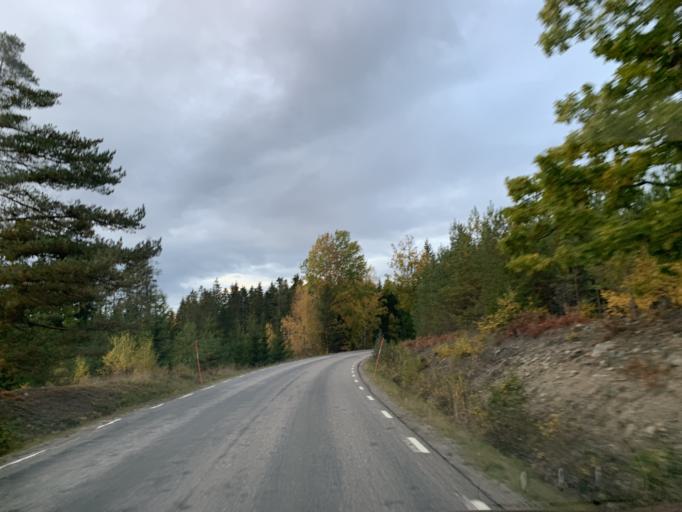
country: SE
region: Stockholm
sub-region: Nynashamns Kommun
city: Osmo
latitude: 58.9374
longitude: 17.7583
